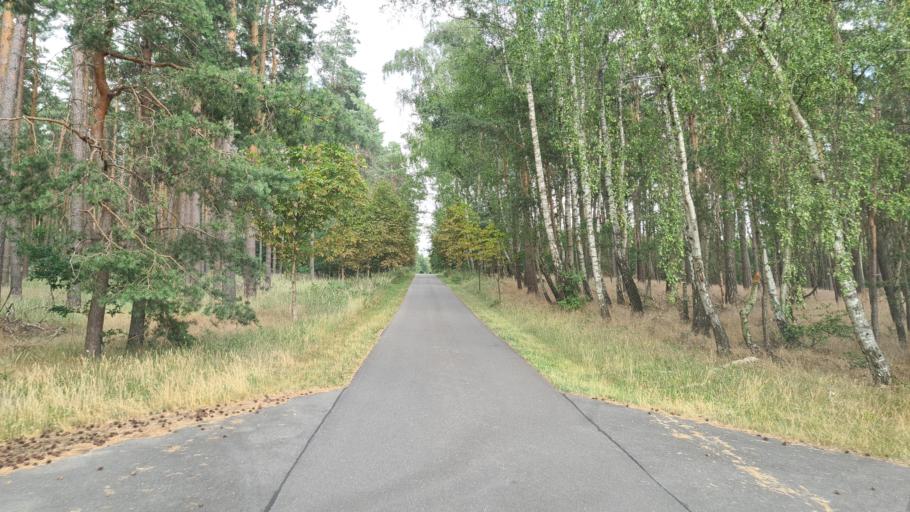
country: DE
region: Brandenburg
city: Niemegk
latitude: 52.0157
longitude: 12.6243
